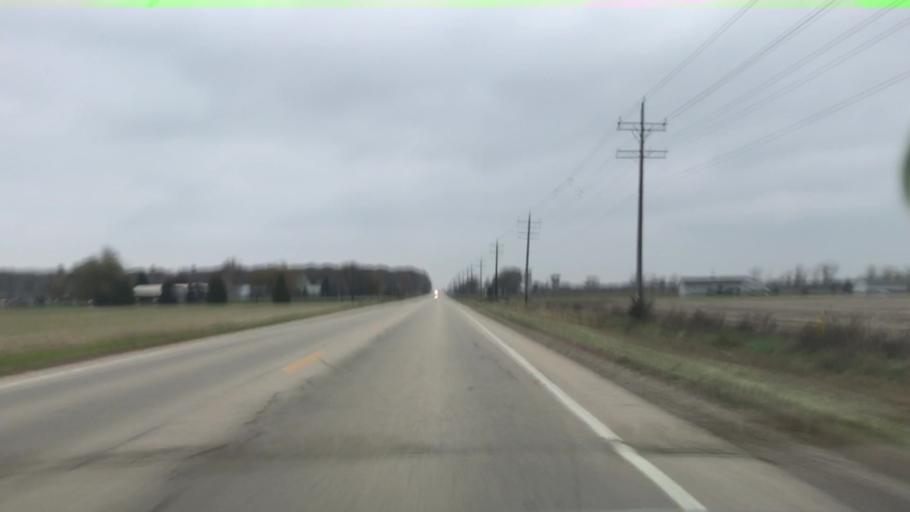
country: US
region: Wisconsin
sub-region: Outagamie County
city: Seymour
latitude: 44.4843
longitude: -88.2911
